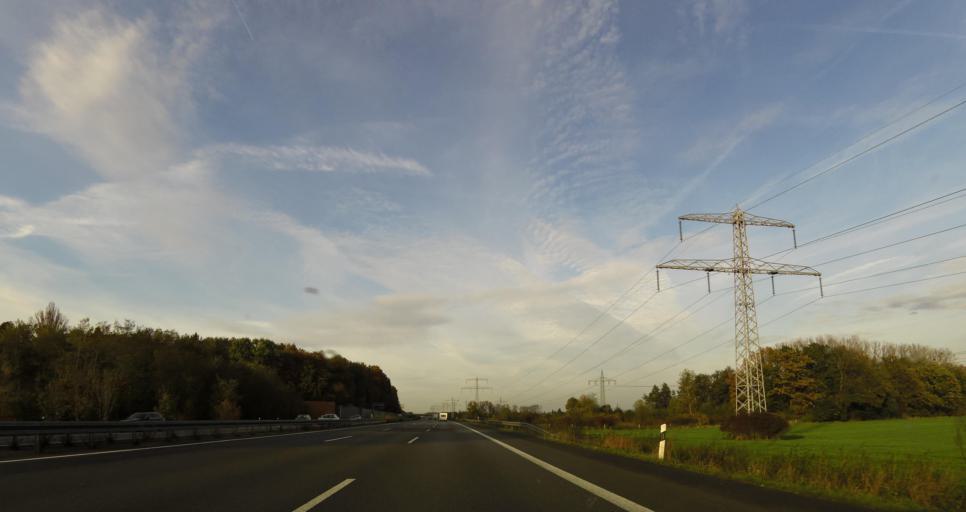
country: DE
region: Lower Saxony
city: Rosdorf
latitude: 51.4956
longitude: 9.8778
